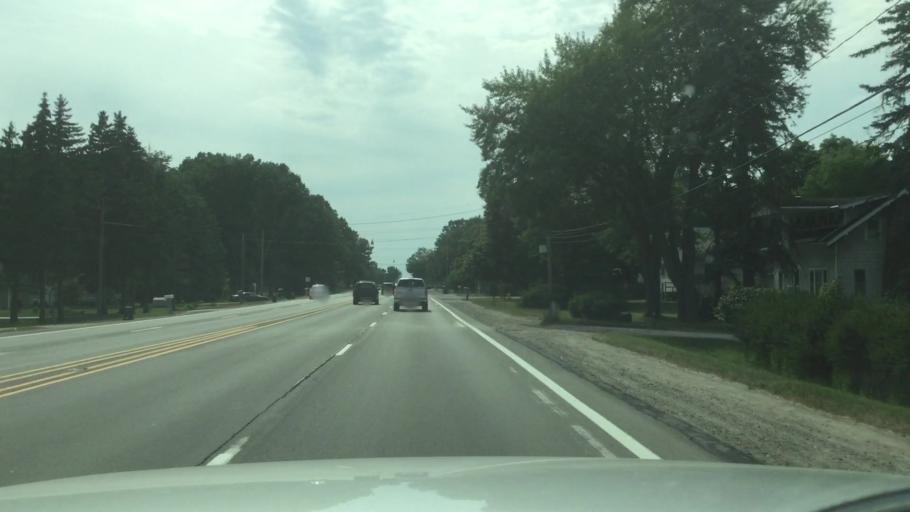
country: US
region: Michigan
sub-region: Genesee County
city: Swartz Creek
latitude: 43.0019
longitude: -83.7884
